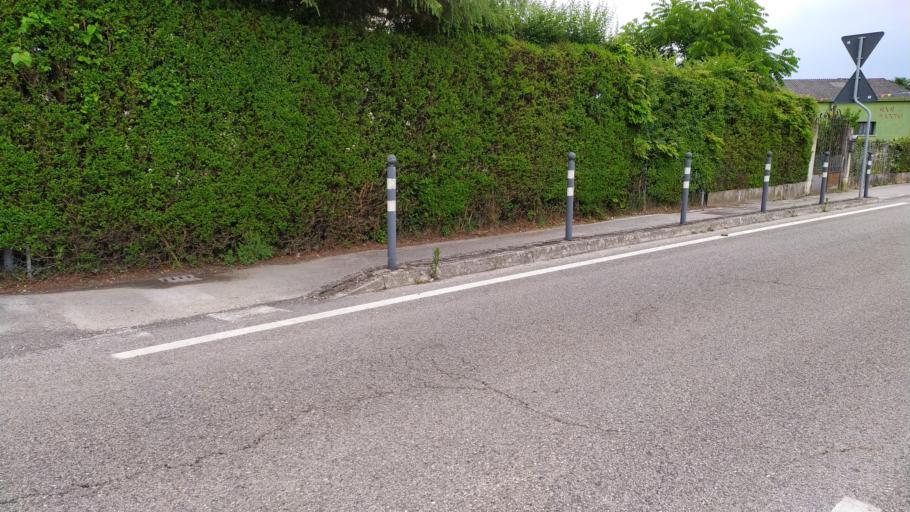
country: IT
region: Veneto
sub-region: Provincia di Padova
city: Abbazia Pisani
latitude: 45.6121
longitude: 11.8552
